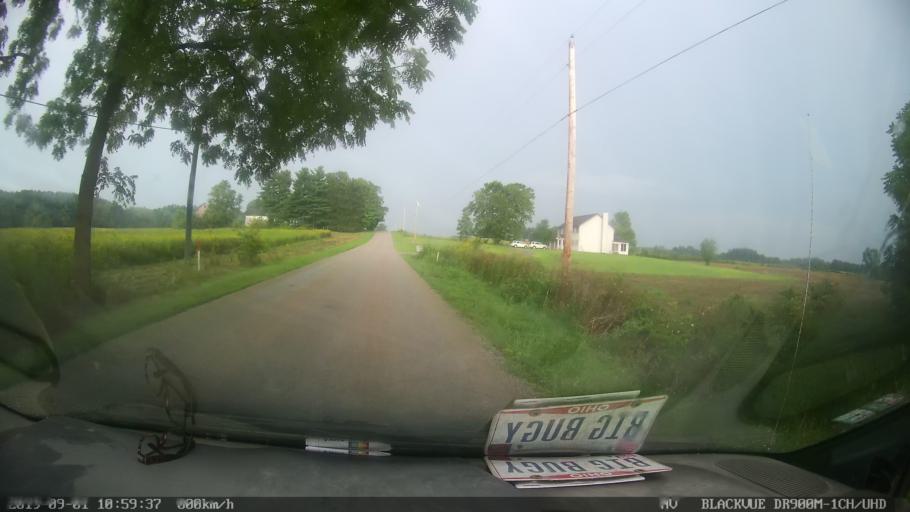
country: US
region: Ohio
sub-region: Morrow County
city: Mount Gilead
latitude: 40.6251
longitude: -82.8103
